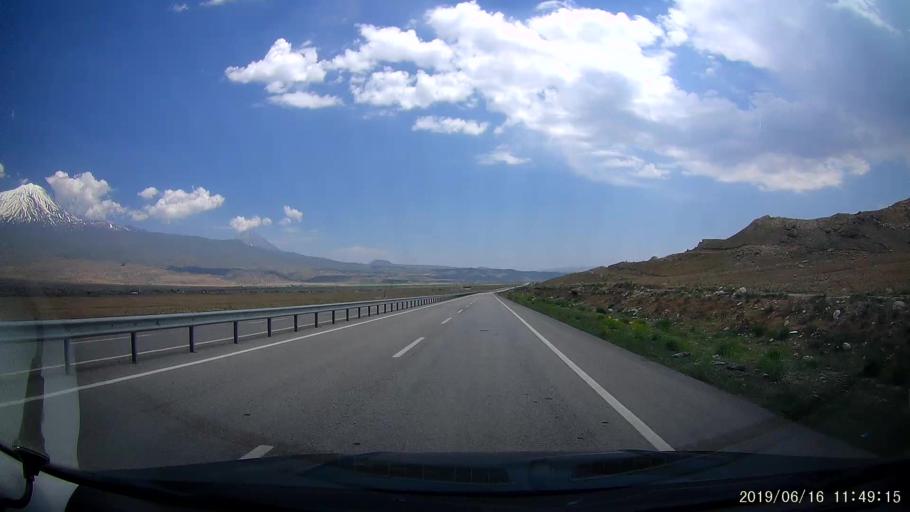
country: TR
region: Agri
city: Dogubayazit
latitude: 39.5574
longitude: 44.1594
